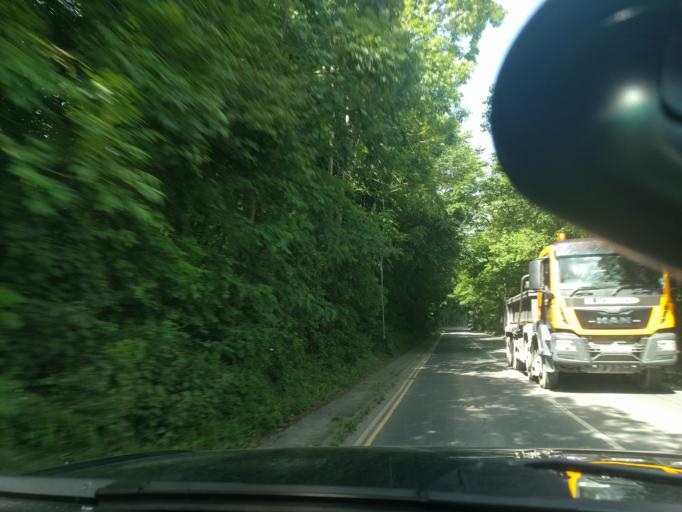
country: GB
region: England
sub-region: Wiltshire
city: Neston
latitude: 51.4264
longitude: -2.2221
